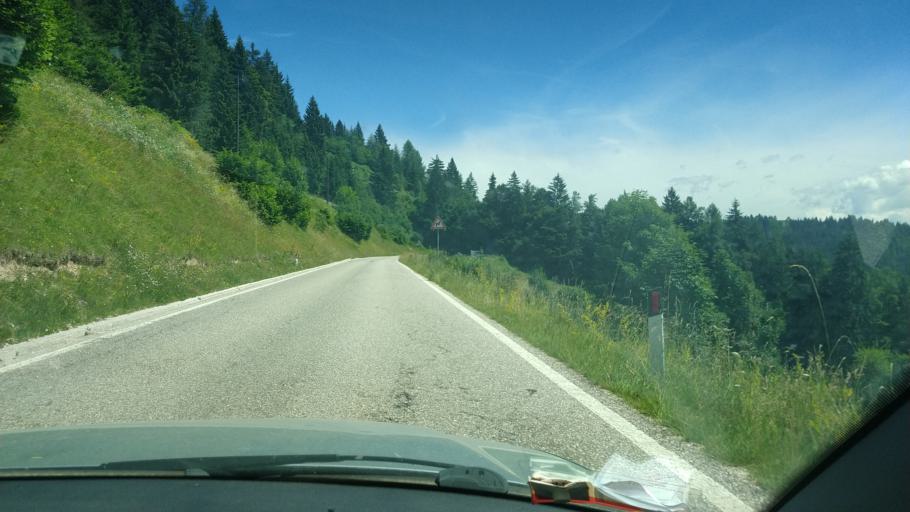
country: IT
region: Trentino-Alto Adige
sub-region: Provincia di Trento
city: Folgaria
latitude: 45.9102
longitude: 11.2074
